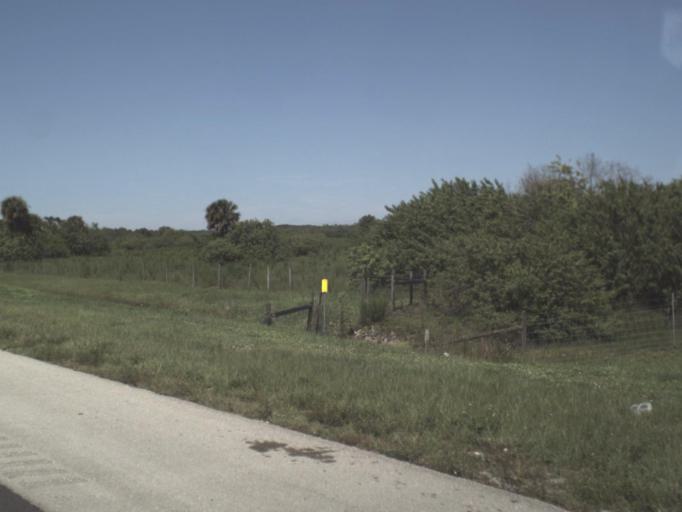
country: US
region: Florida
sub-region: Lee County
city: Bonita Springs
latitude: 26.3607
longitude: -81.7613
